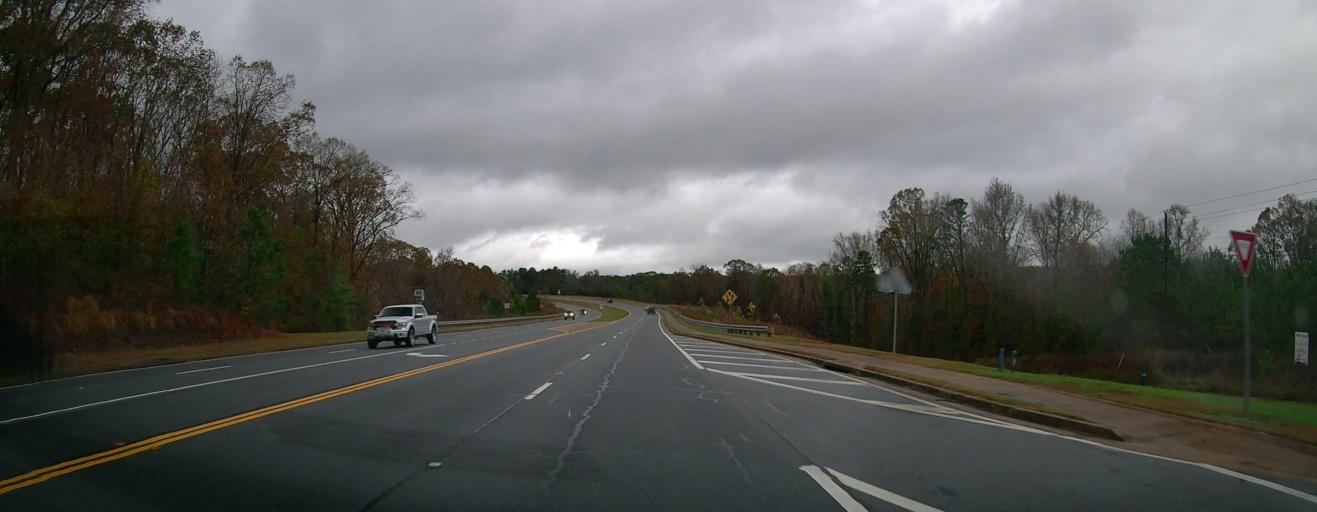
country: US
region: Georgia
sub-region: Jackson County
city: Nicholson
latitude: 34.1263
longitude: -83.4289
